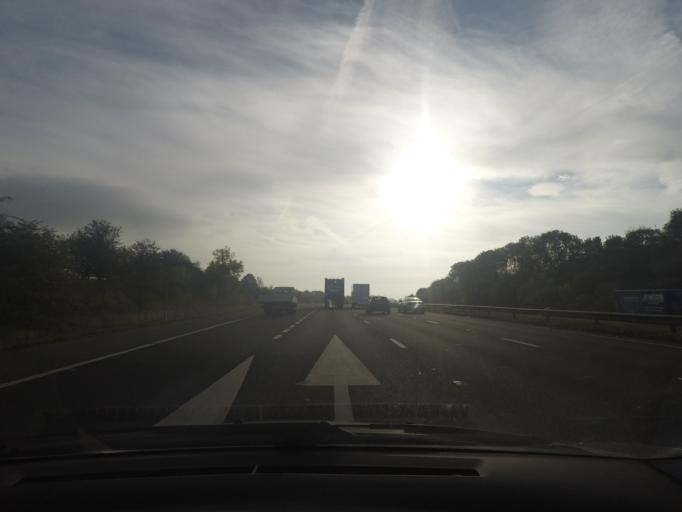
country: GB
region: England
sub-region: Barnsley
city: Dodworth
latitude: 53.5537
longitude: -1.5235
